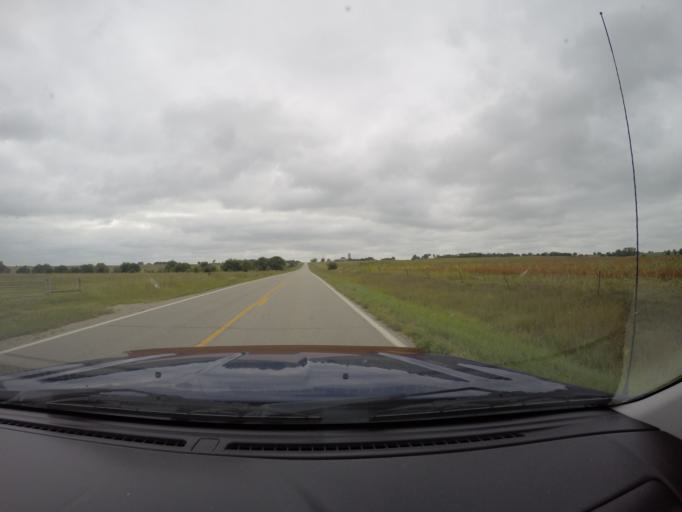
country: US
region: Kansas
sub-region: Morris County
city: Council Grove
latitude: 38.7976
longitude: -96.6961
